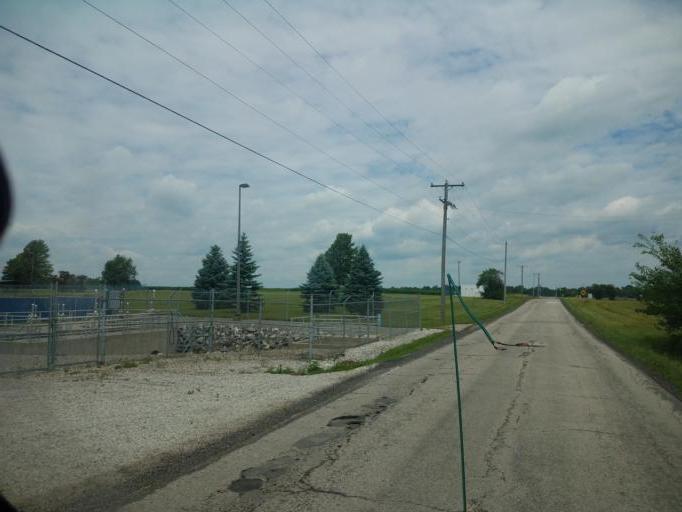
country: US
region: Ohio
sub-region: Crawford County
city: Crestline
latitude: 40.7891
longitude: -82.6976
